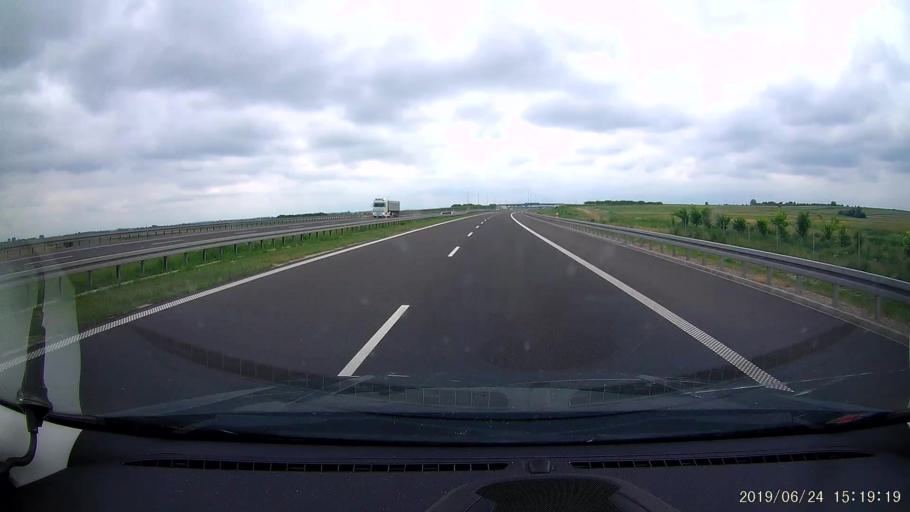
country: PL
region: Subcarpathian Voivodeship
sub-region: Powiat przeworski
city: Mirocin
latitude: 50.0560
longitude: 22.5694
